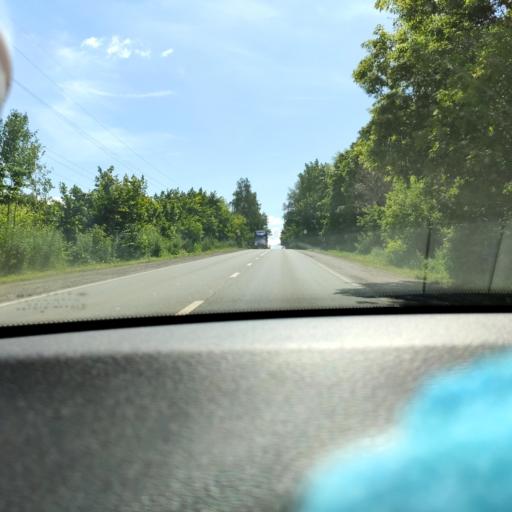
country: RU
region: Samara
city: Novosemeykino
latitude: 53.3421
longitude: 50.2467
